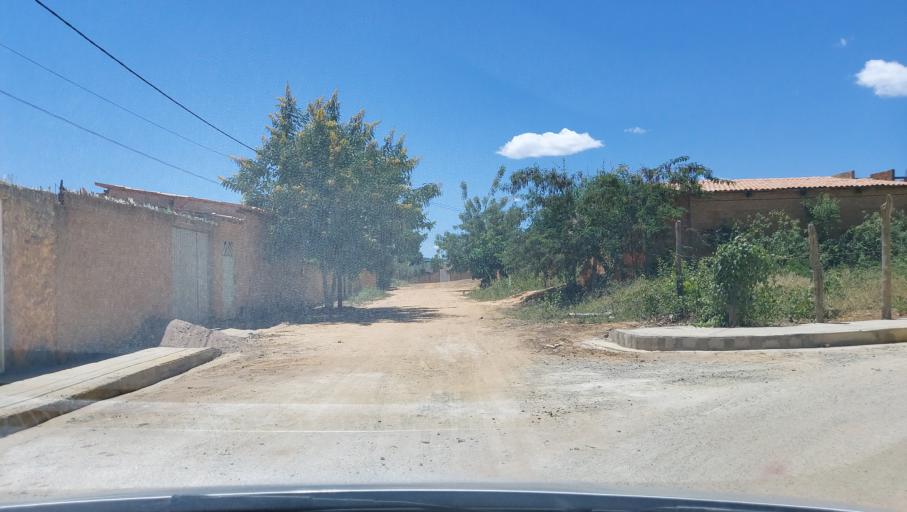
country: BR
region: Bahia
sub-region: Oliveira Dos Brejinhos
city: Beira Rio
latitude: -12.0033
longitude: -42.6297
